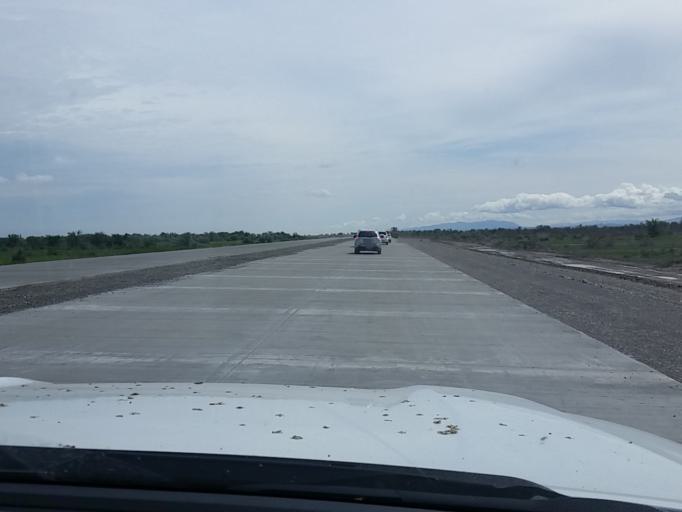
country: KZ
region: Almaty Oblysy
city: Turgen'
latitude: 43.6094
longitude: 78.3278
